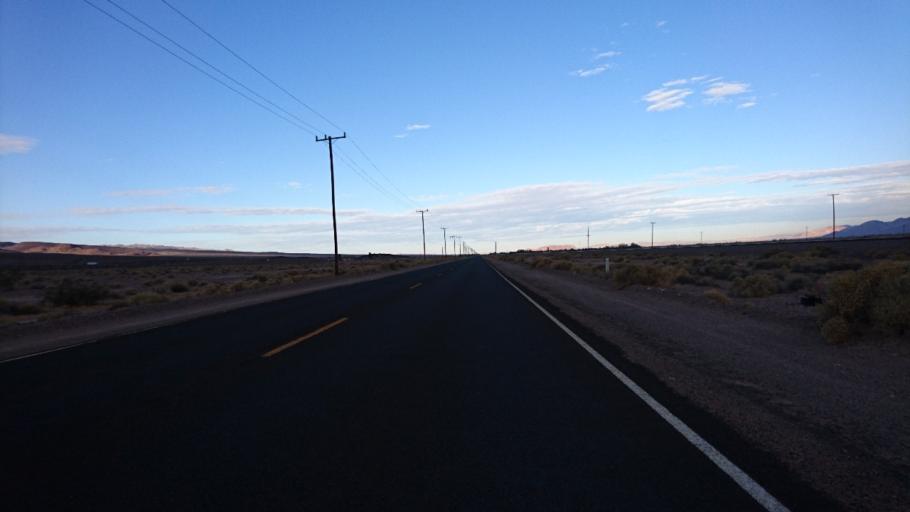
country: US
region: California
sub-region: San Bernardino County
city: Barstow
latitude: 34.8358
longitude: -116.7113
